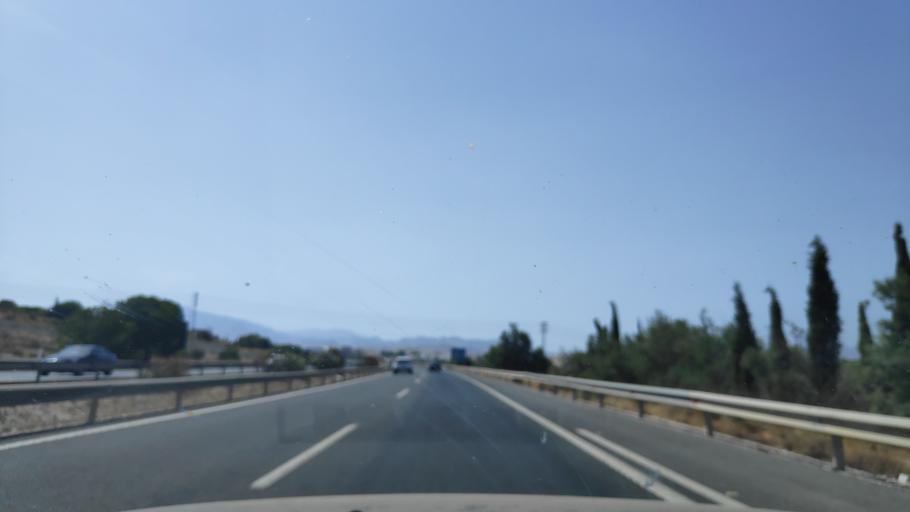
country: ES
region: Murcia
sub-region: Murcia
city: Molina de Segura
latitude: 38.0763
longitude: -1.2072
